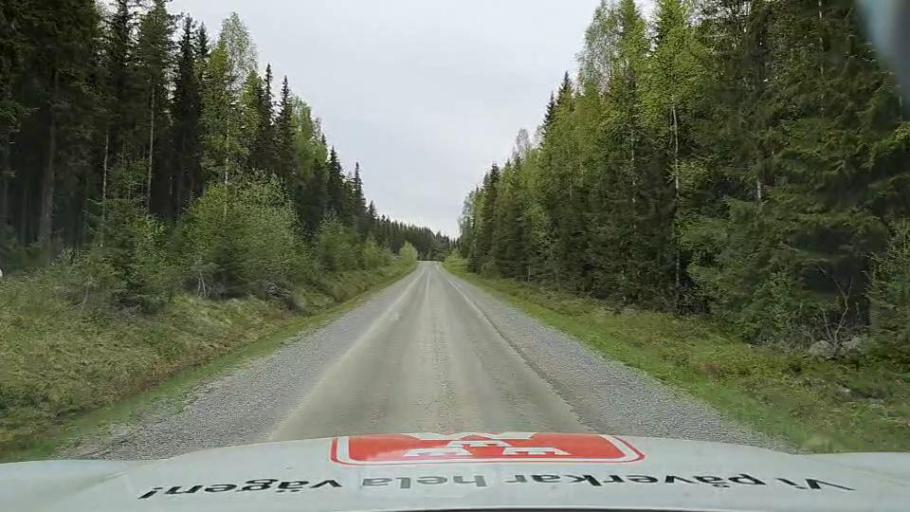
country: SE
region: Jaemtland
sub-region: OEstersunds Kommun
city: Brunflo
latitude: 62.6489
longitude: 14.9262
